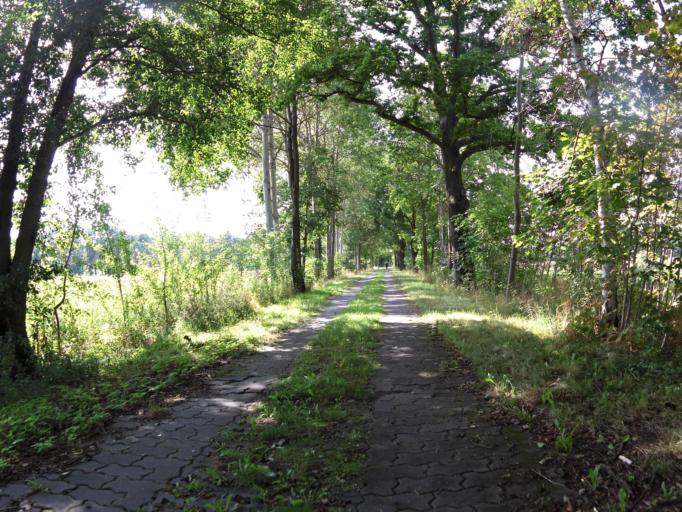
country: DE
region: Brandenburg
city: Storkow
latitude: 52.2369
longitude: 13.8846
